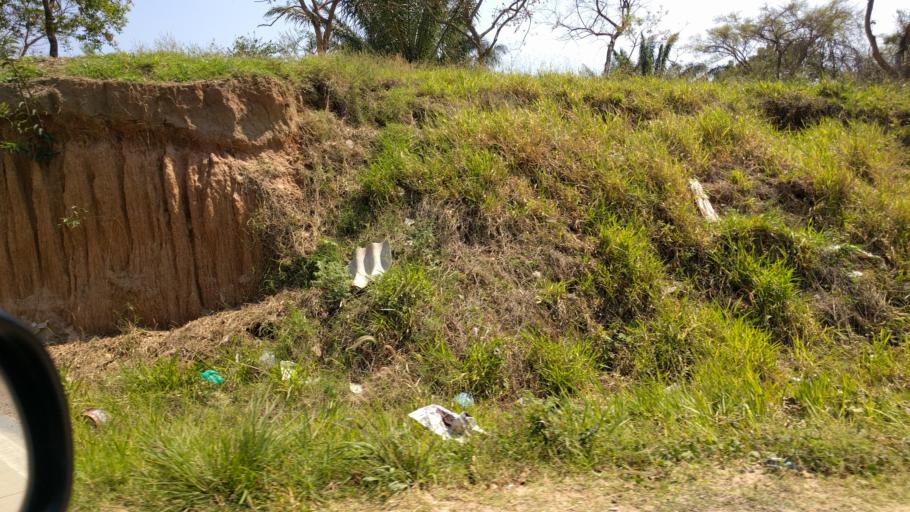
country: BO
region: Santa Cruz
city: Santa Cruz de la Sierra
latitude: -17.7615
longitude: -63.2284
